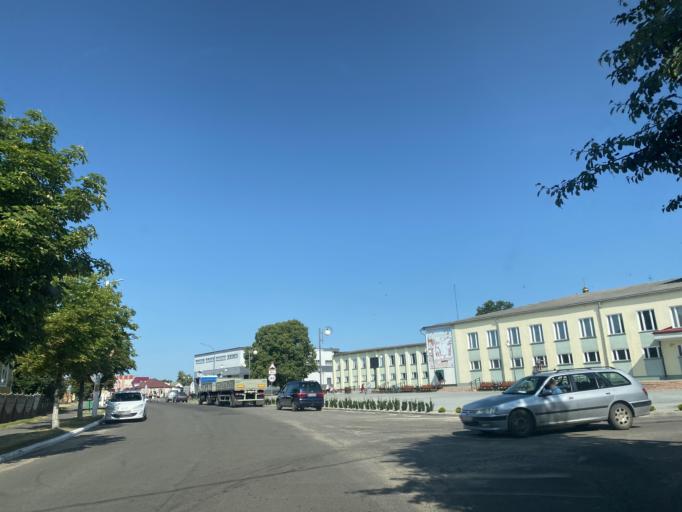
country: BY
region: Brest
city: Ivanava
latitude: 52.3163
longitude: 25.6105
